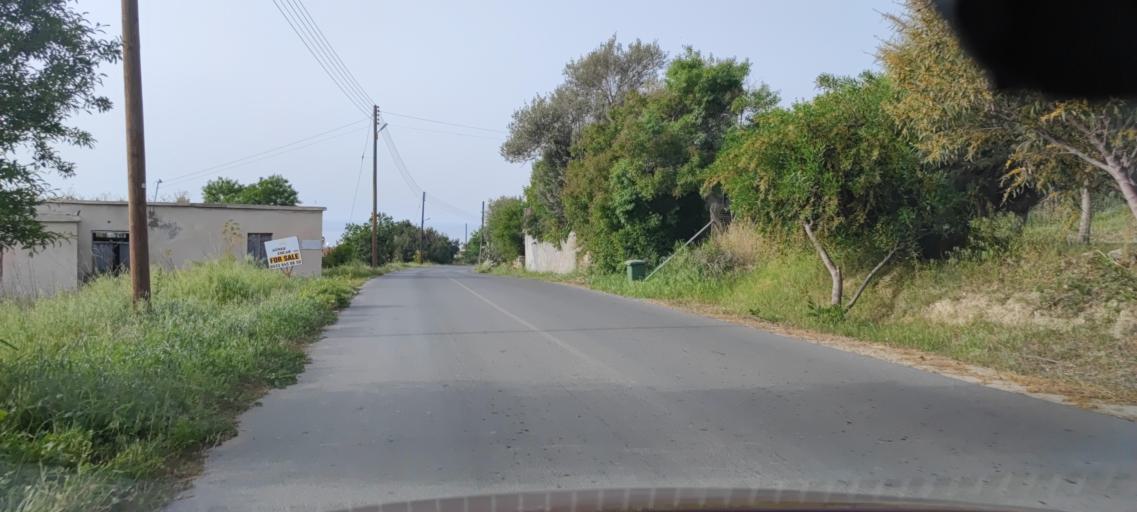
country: CY
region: Ammochostos
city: Leonarisso
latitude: 35.5374
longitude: 34.1933
